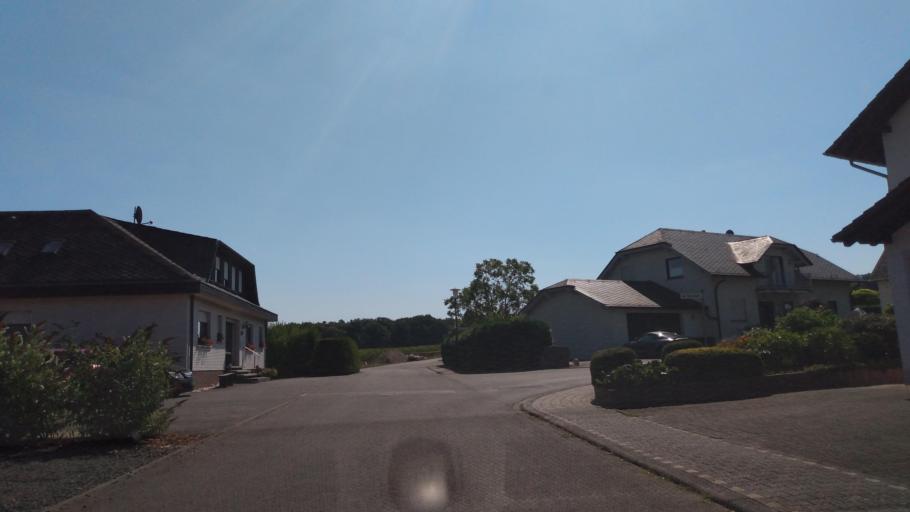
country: DE
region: Rheinland-Pfalz
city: Kleinich
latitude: 49.8896
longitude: 7.1852
